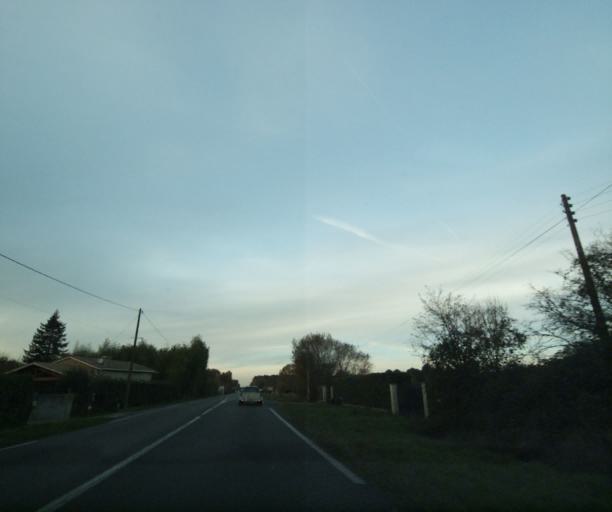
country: FR
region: Aquitaine
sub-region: Departement de la Gironde
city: Bazas
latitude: 44.4888
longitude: -0.2334
